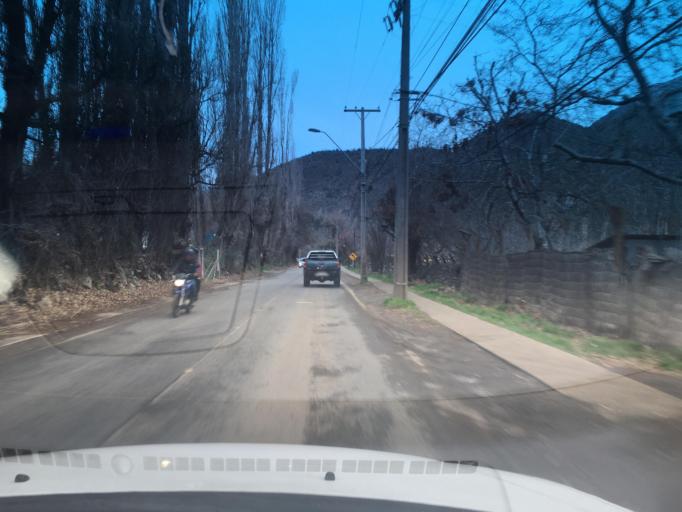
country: CL
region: Santiago Metropolitan
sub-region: Provincia de Cordillera
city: Puente Alto
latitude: -33.7310
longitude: -70.3146
